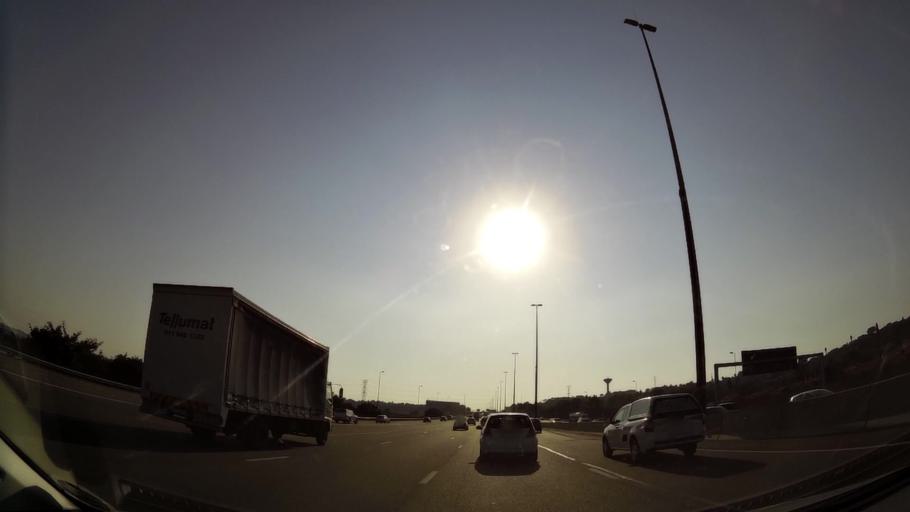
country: ZA
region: Gauteng
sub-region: City of Tshwane Metropolitan Municipality
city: Centurion
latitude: -25.8263
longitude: 28.2464
